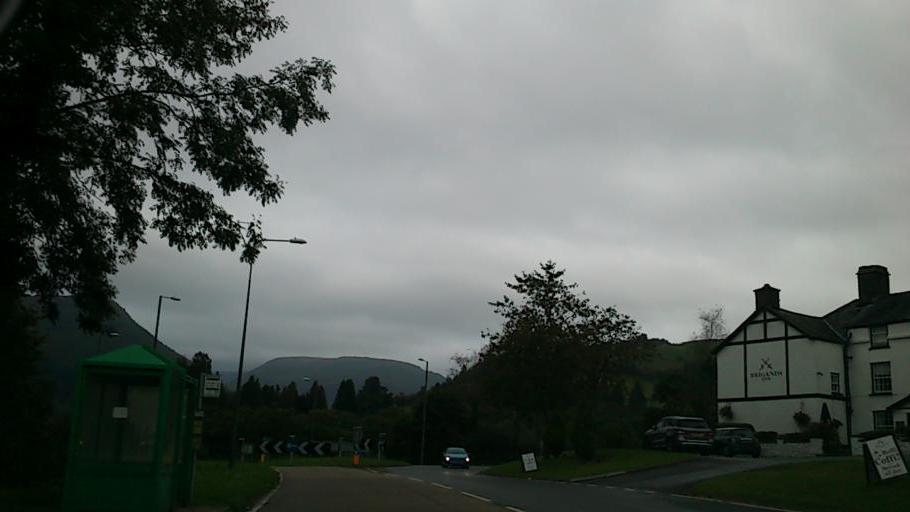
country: GB
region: Wales
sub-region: Gwynedd
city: Corris
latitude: 52.6977
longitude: -3.6844
